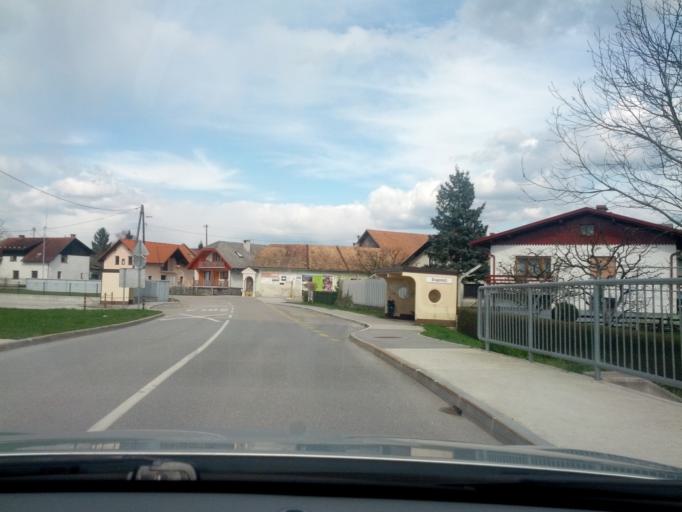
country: SI
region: Dol pri Ljubljani
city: Dol pri Ljubljani
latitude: 46.1061
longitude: 14.5938
